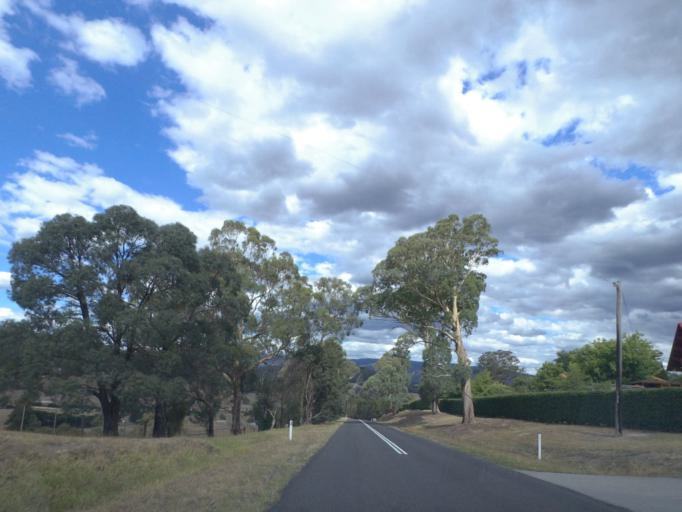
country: AU
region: Victoria
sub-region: Yarra Ranges
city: Healesville
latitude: -37.6455
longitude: 145.4596
